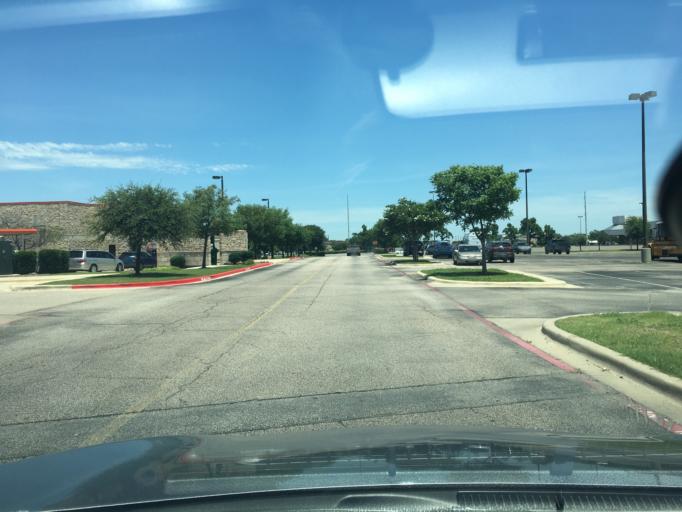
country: US
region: Texas
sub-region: Dallas County
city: Richardson
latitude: 32.9421
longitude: -96.6991
